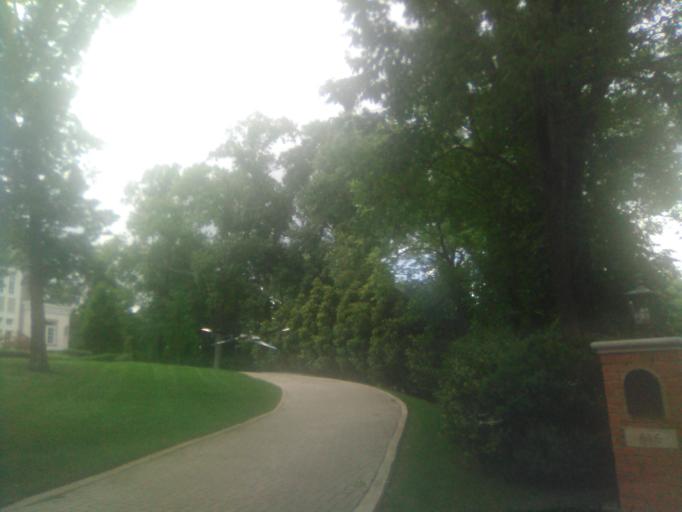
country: US
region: Tennessee
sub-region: Davidson County
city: Belle Meade
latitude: 36.1011
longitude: -86.8477
